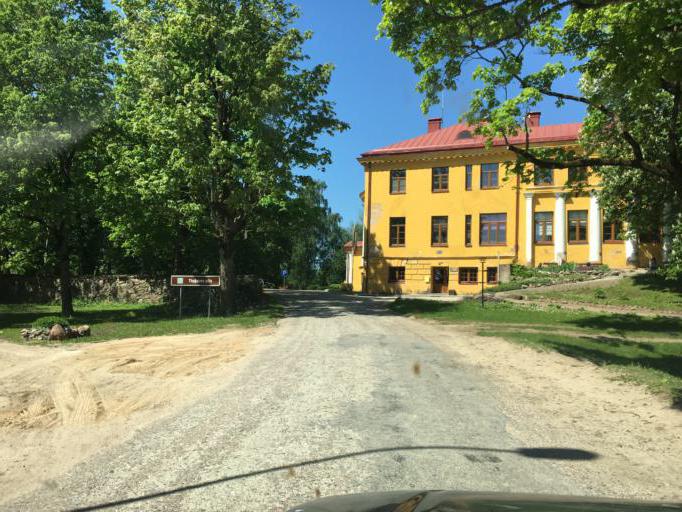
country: LV
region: Talsu Rajons
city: Valdemarpils
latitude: 57.4494
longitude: 22.5266
